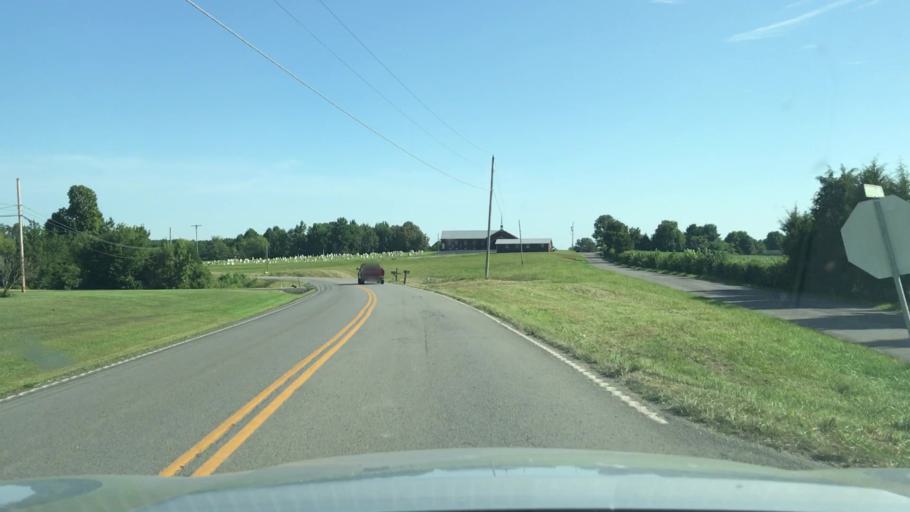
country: US
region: Kentucky
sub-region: Muhlenberg County
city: Greenville
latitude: 37.1774
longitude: -87.1525
